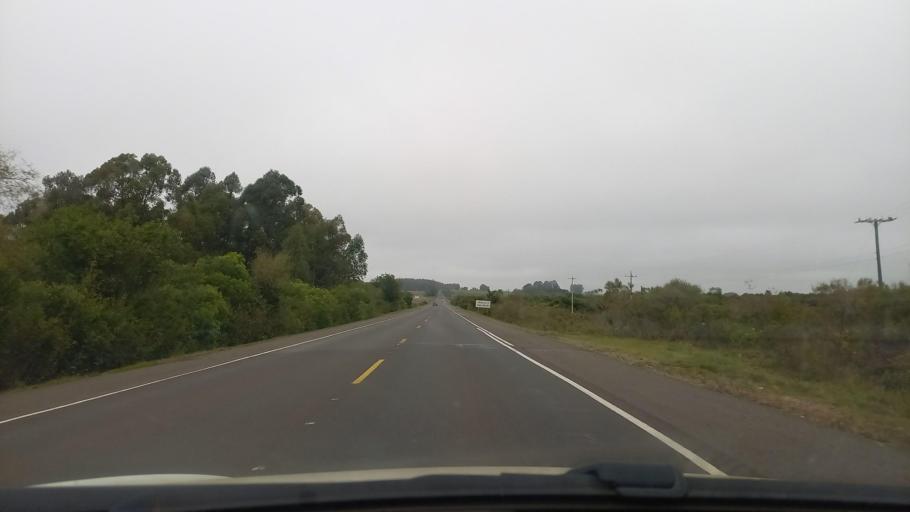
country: BR
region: Rio Grande do Sul
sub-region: Rosario Do Sul
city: Rosario do Sul
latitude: -30.3111
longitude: -54.9963
